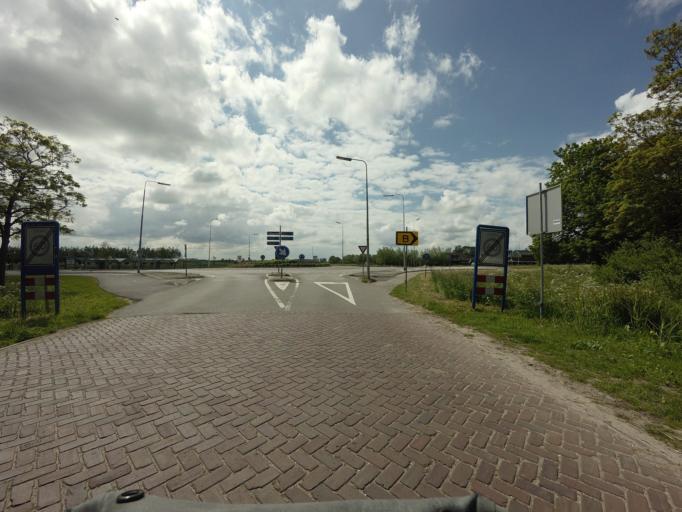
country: NL
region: South Holland
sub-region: Gemeente Giessenlanden
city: Giessenburg
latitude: 51.9010
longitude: 4.9390
